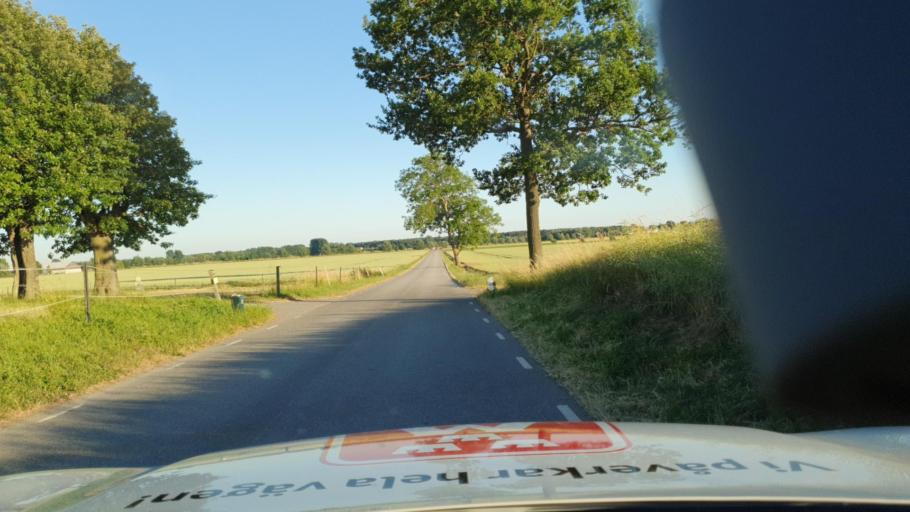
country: SE
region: Skane
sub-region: Lomma Kommun
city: Lomma
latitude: 55.7076
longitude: 13.0592
